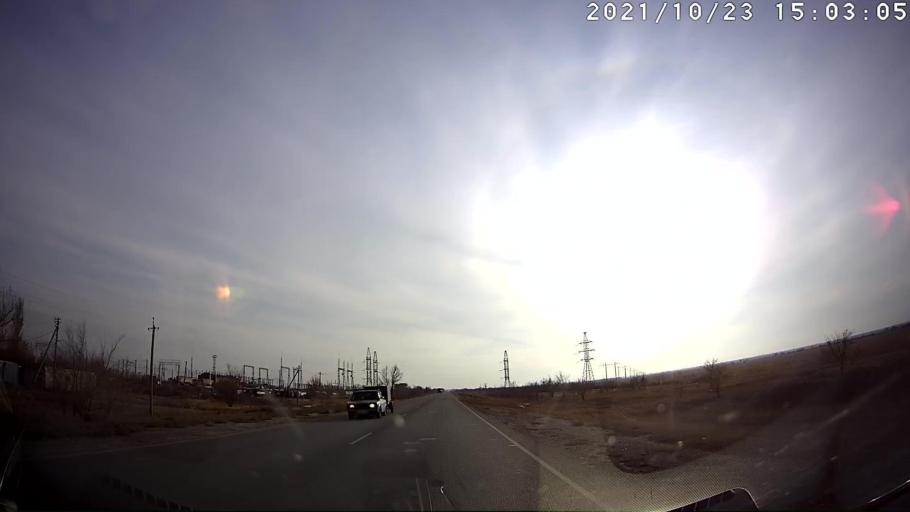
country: RU
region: Volgograd
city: Volgograd
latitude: 48.4181
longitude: 44.3795
